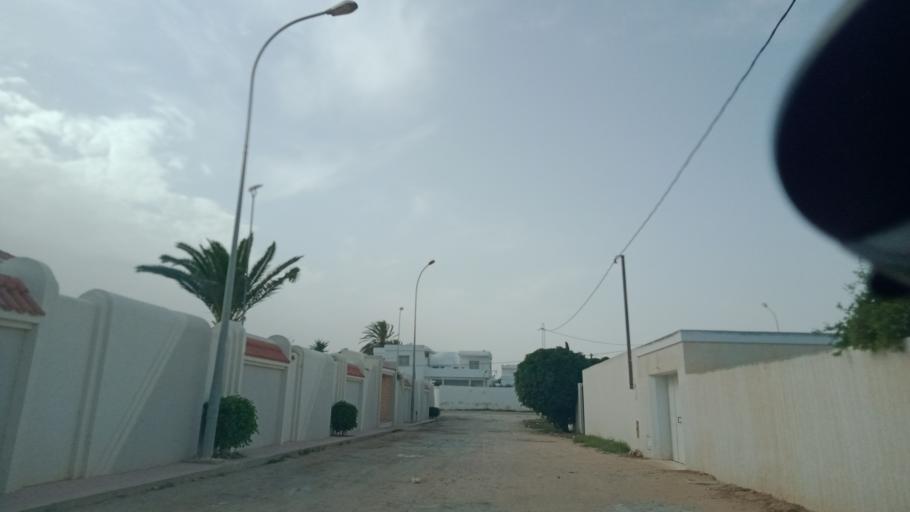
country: TN
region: Safaqis
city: Al Qarmadah
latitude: 34.7847
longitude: 10.7626
